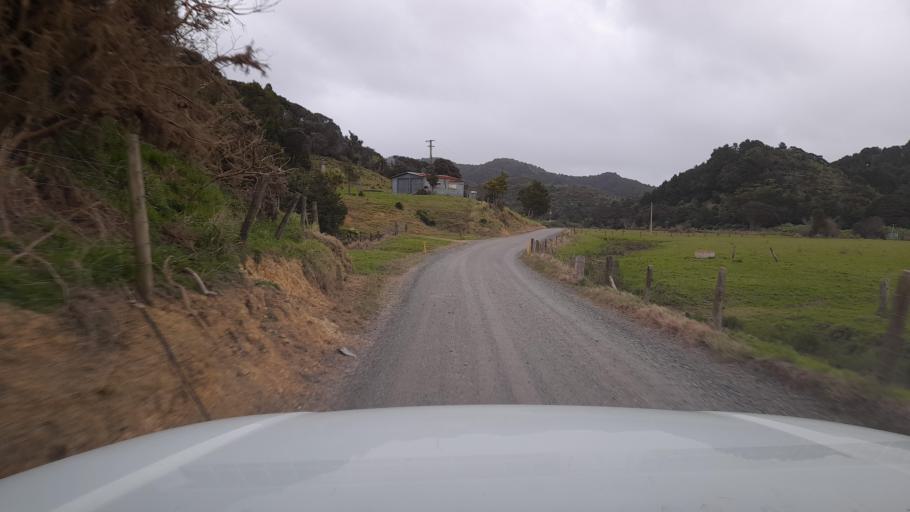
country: NZ
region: Northland
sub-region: Far North District
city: Paihia
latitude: -35.3453
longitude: 174.2291
